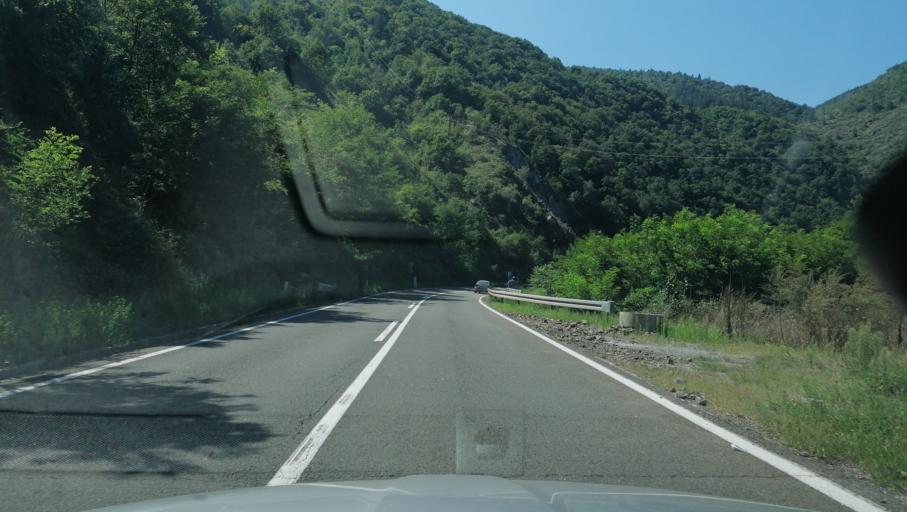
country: RS
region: Central Serbia
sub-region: Raski Okrug
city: Kraljevo
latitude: 43.5956
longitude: 20.5620
